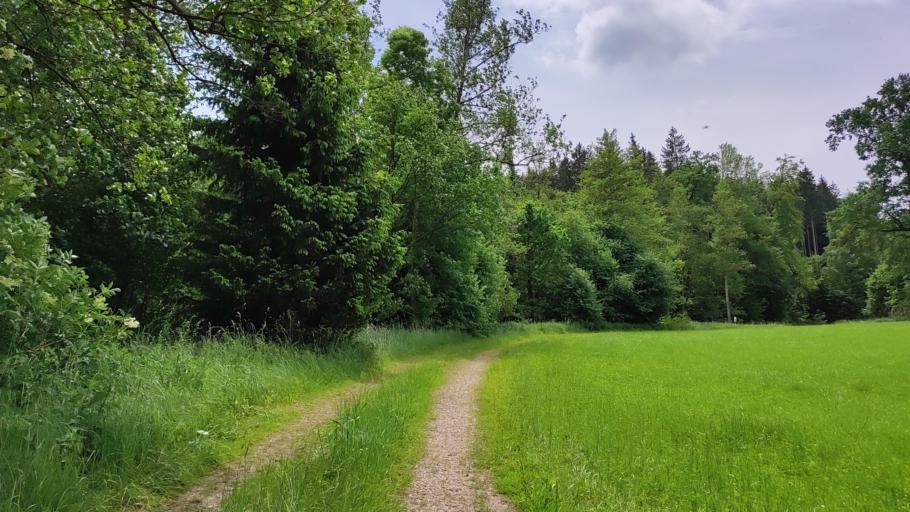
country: DE
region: Bavaria
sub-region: Swabia
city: Landensberg
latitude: 48.4291
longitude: 10.5093
